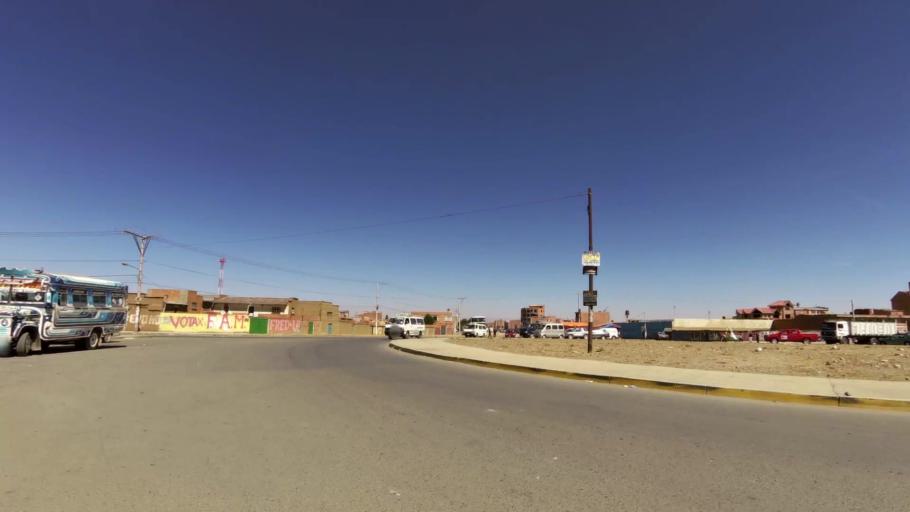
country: BO
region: La Paz
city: La Paz
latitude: -16.5311
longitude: -68.2101
